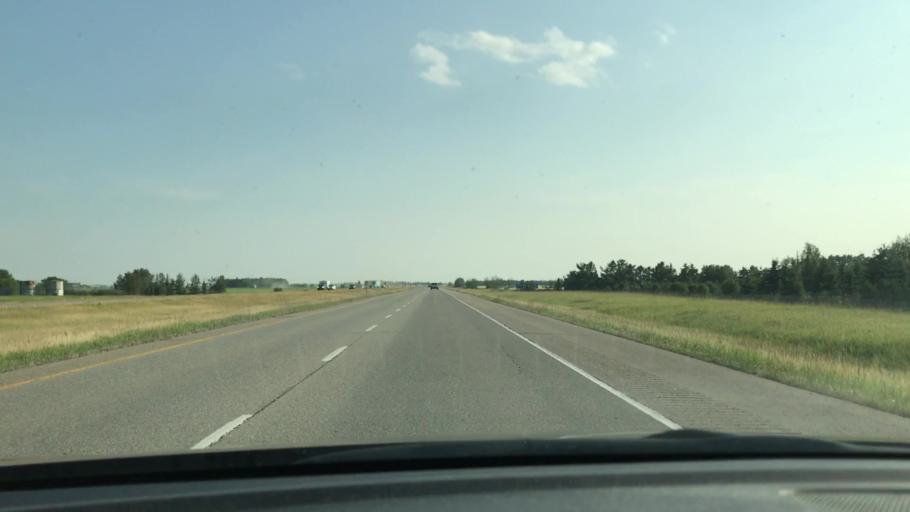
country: CA
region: Alberta
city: Leduc
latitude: 53.2197
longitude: -113.5816
